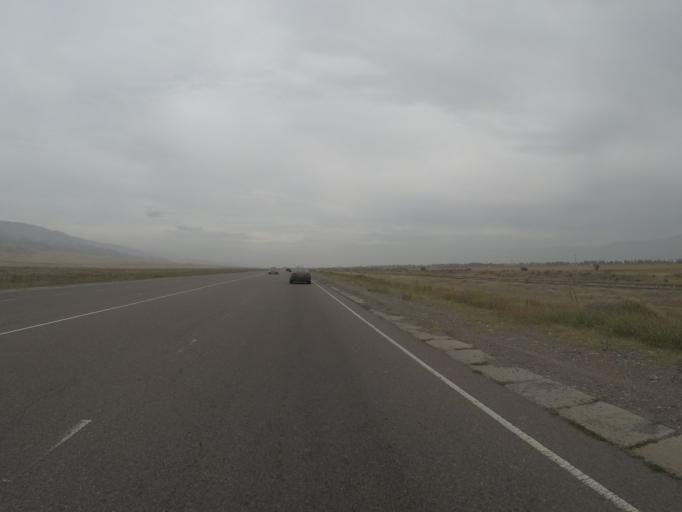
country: KG
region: Chuy
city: Tokmok
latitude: 42.8298
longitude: 75.4943
